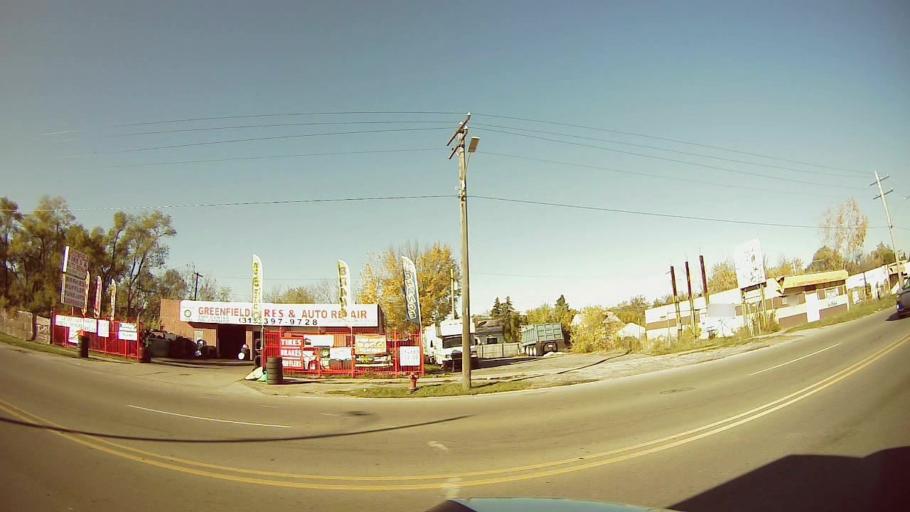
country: US
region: Michigan
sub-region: Wayne County
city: Dearborn
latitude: 42.3619
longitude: -83.1970
